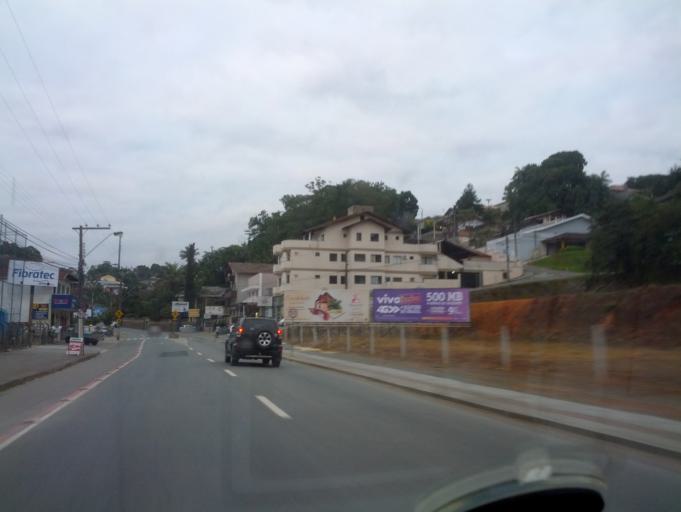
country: BR
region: Santa Catarina
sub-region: Blumenau
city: Blumenau
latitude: -26.8814
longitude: -49.0819
